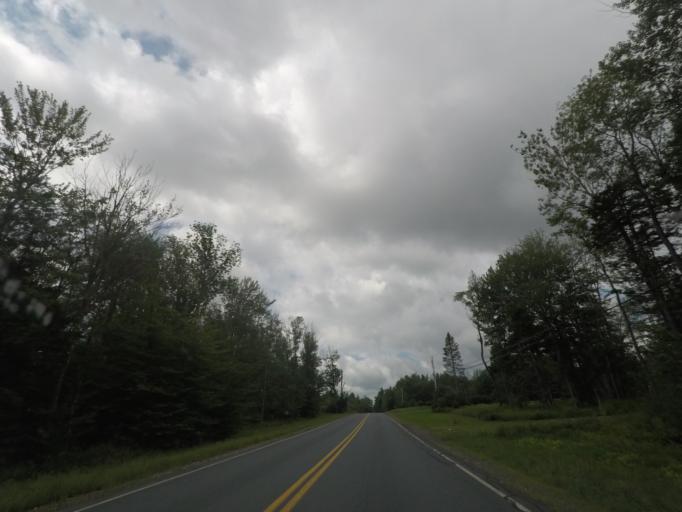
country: US
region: New York
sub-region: Rensselaer County
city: Poestenkill
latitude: 42.6971
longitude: -73.4112
